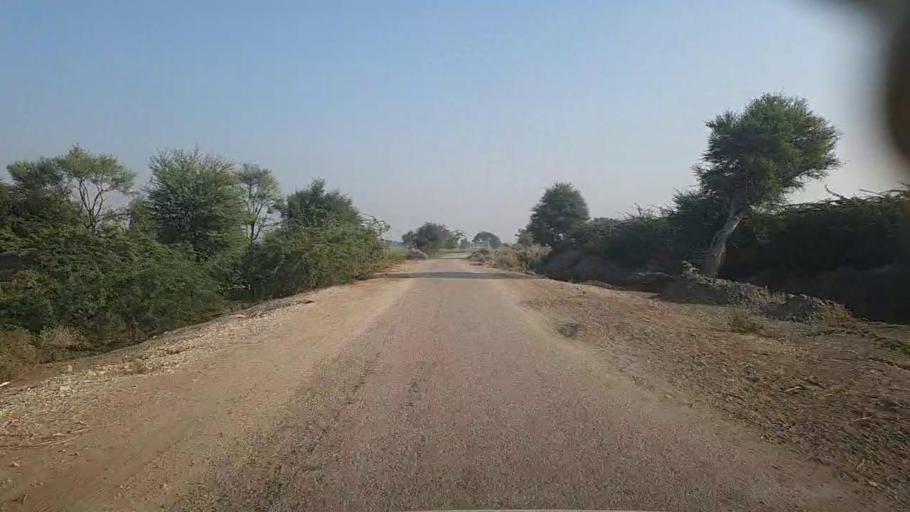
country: PK
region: Sindh
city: Karaundi
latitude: 26.7399
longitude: 68.4787
